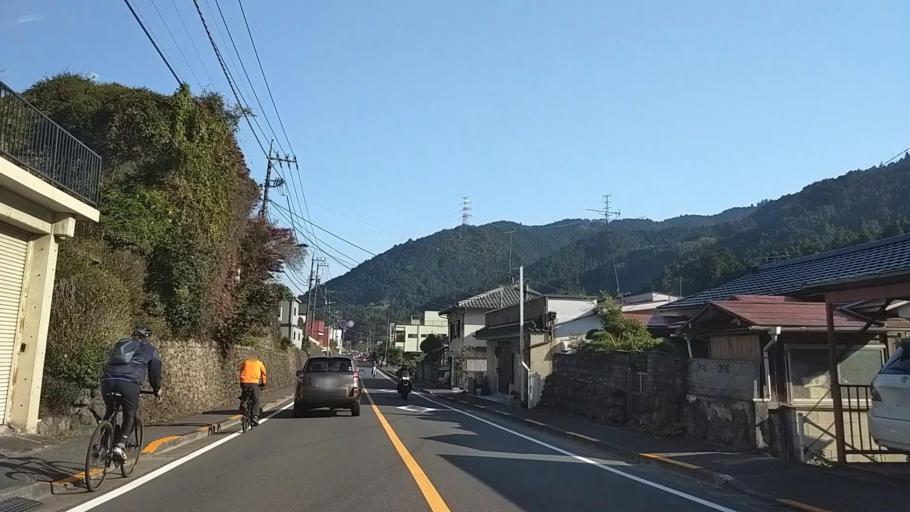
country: JP
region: Tokyo
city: Ome
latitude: 35.8054
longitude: 139.1904
